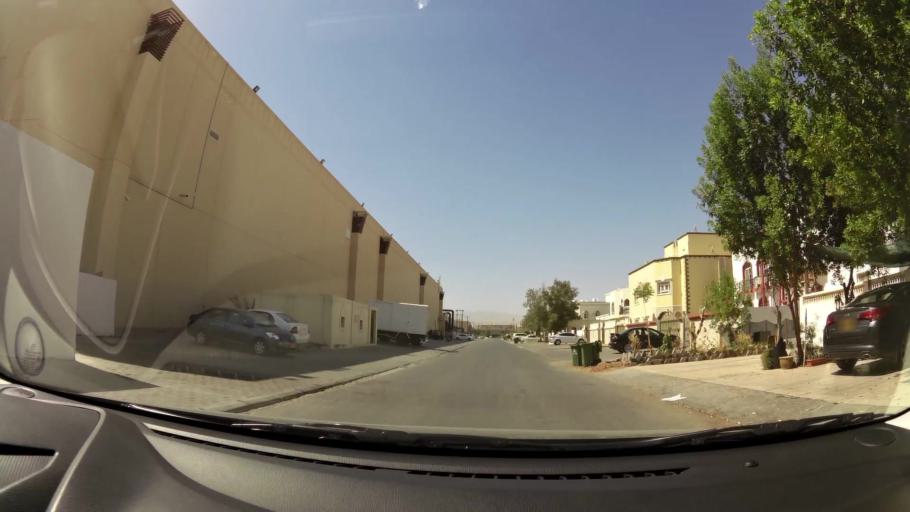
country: OM
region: Muhafazat Masqat
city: As Sib al Jadidah
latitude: 23.6003
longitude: 58.2462
